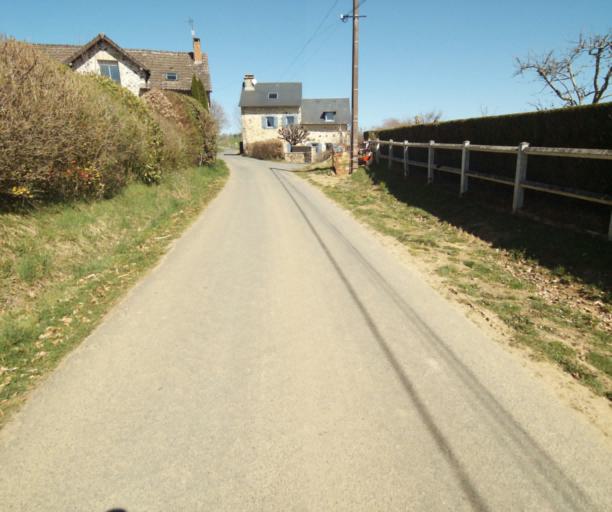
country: FR
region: Limousin
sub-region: Departement de la Correze
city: Saint-Clement
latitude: 45.3263
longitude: 1.7107
